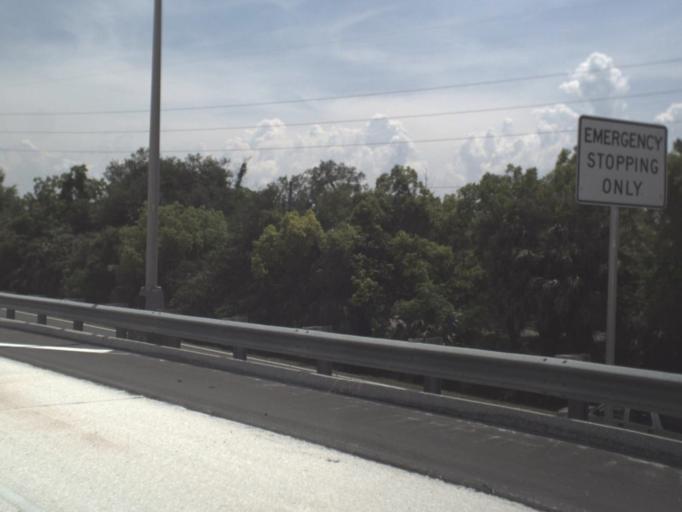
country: US
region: Florida
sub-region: Duval County
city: Jacksonville
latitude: 30.3334
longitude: -81.6371
